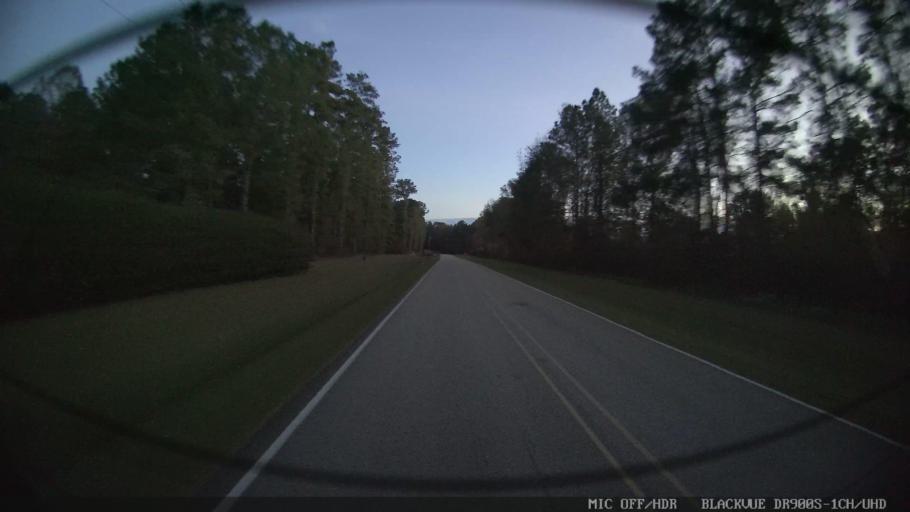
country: US
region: Mississippi
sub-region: Perry County
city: New Augusta
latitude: 31.1590
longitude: -89.2116
